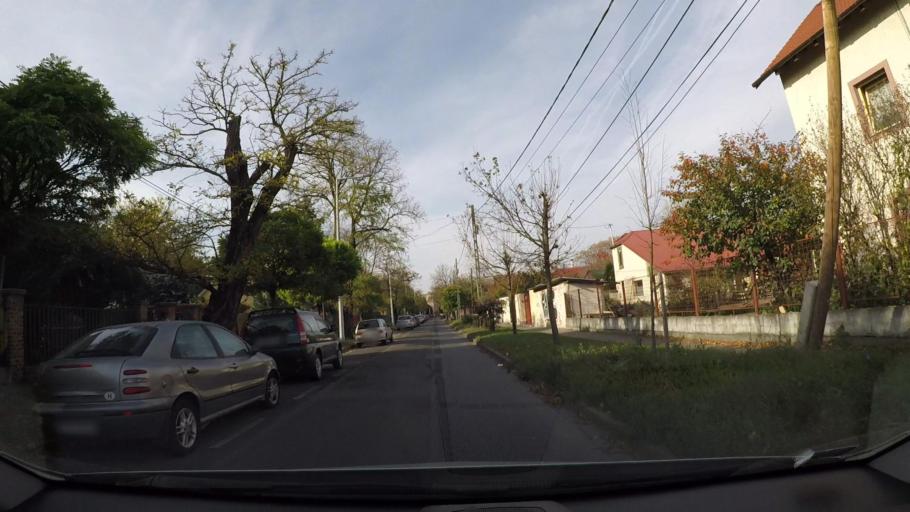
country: HU
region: Budapest
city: Budapest X. keruelet
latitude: 47.4781
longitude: 19.1571
